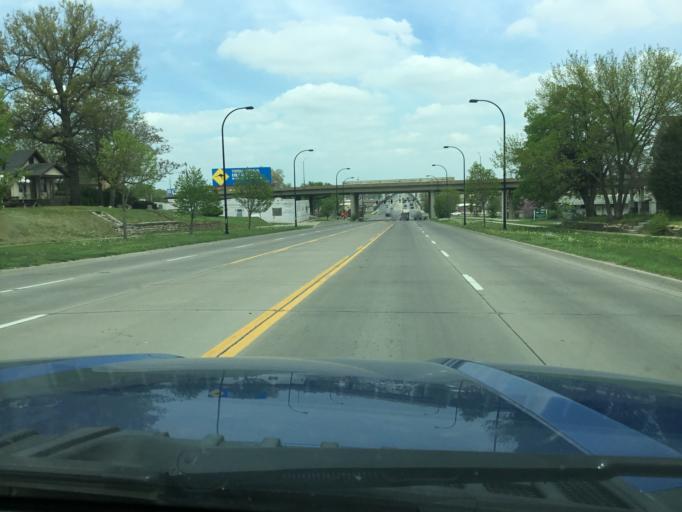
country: US
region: Kansas
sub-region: Shawnee County
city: Topeka
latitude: 39.0578
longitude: -95.6770
